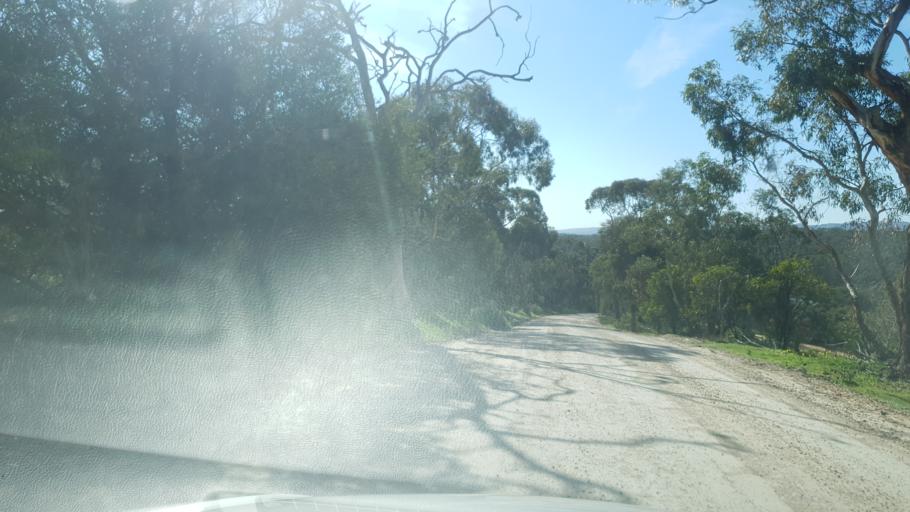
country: AU
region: South Australia
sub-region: Barossa
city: Williamstown
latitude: -34.6542
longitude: 138.8285
